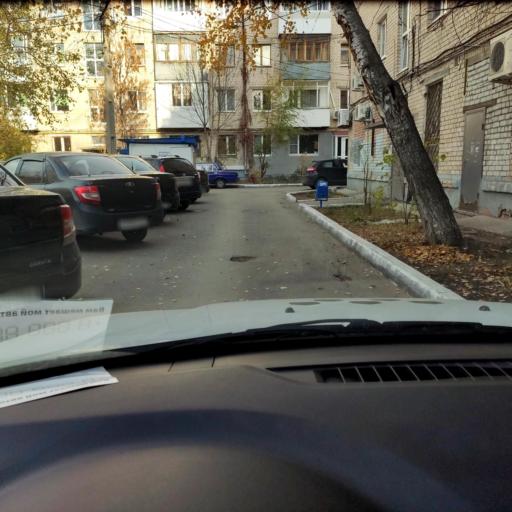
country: RU
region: Samara
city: Tol'yatti
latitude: 53.5086
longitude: 49.4152
